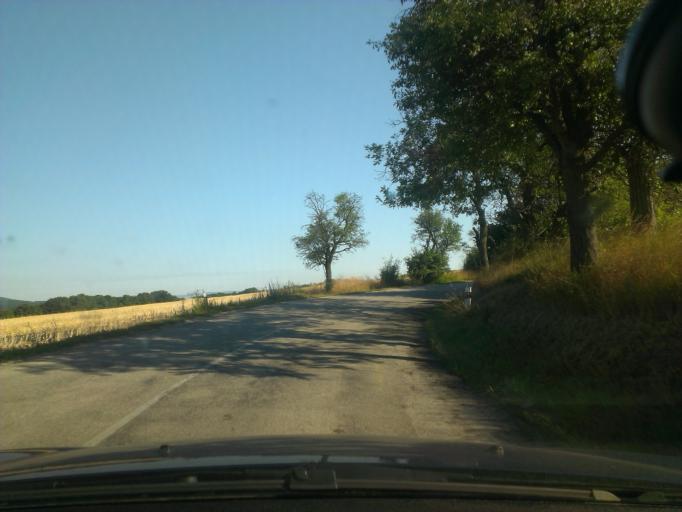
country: SK
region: Trnavsky
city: Vrbove
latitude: 48.6728
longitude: 17.6915
